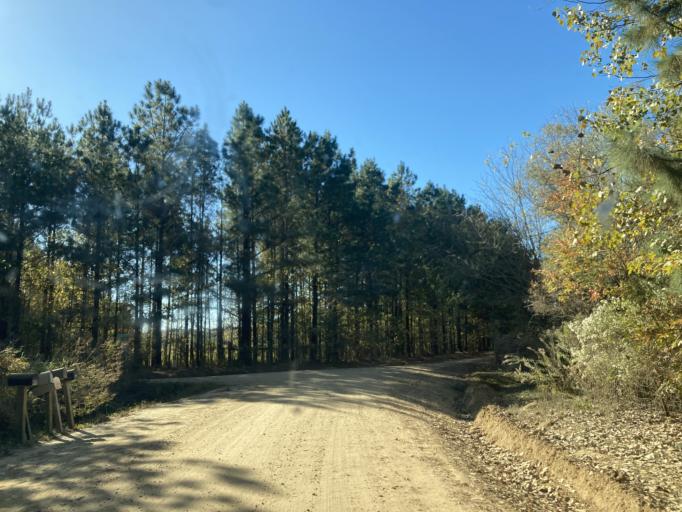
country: US
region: Mississippi
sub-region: Madison County
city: Kearney Park
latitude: 32.6720
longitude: -90.3411
